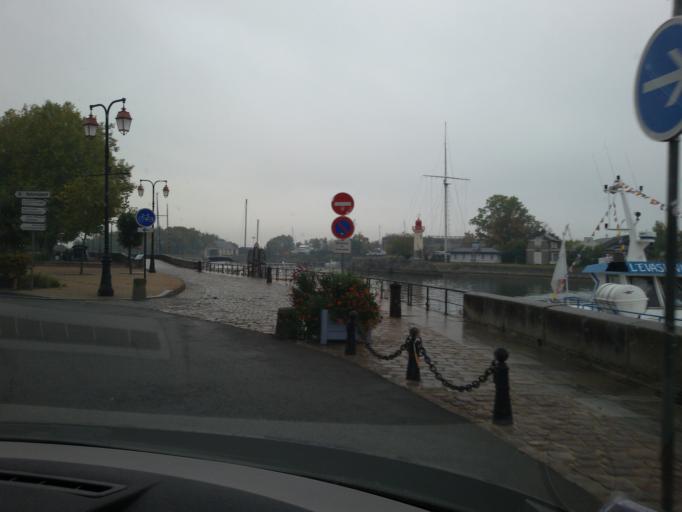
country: FR
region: Lower Normandy
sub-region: Departement du Calvados
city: Honfleur
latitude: 49.4218
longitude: 0.2341
